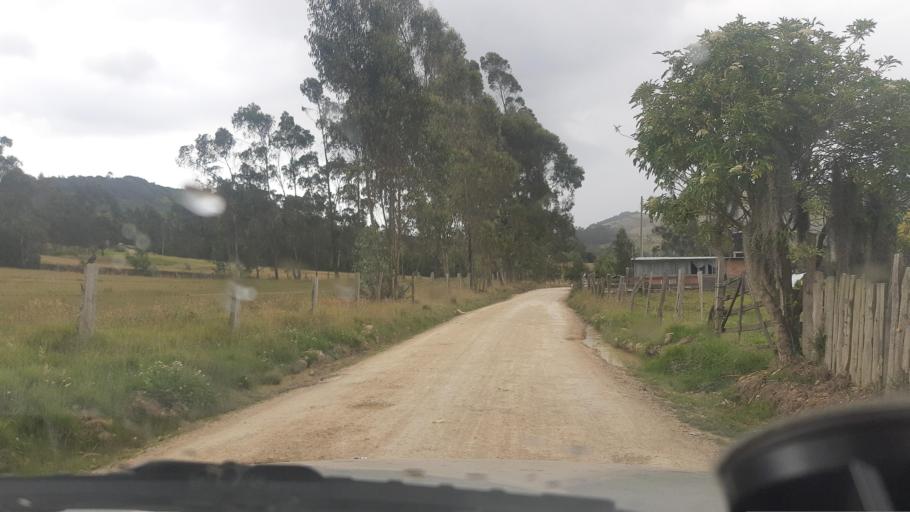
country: CO
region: Cundinamarca
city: Cucunuba
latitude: 5.1905
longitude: -73.7947
